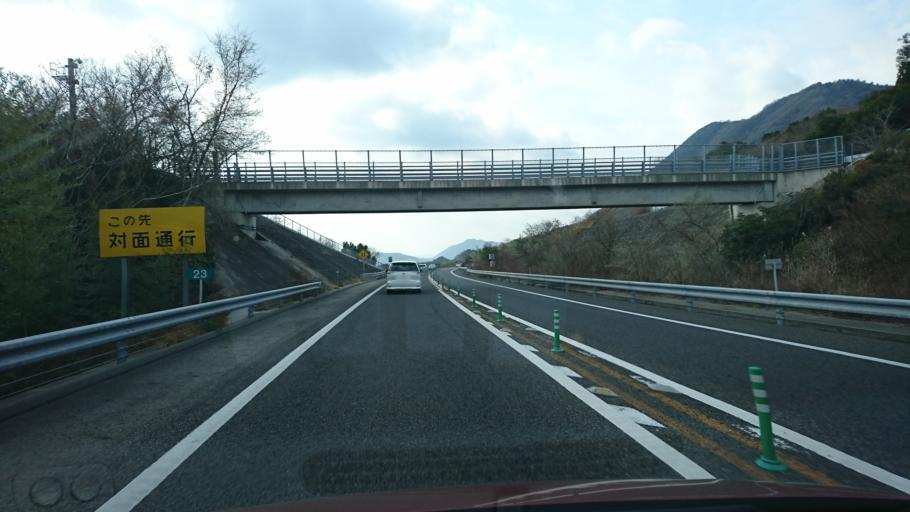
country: JP
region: Hiroshima
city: Innoshima
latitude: 34.2745
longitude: 133.1061
